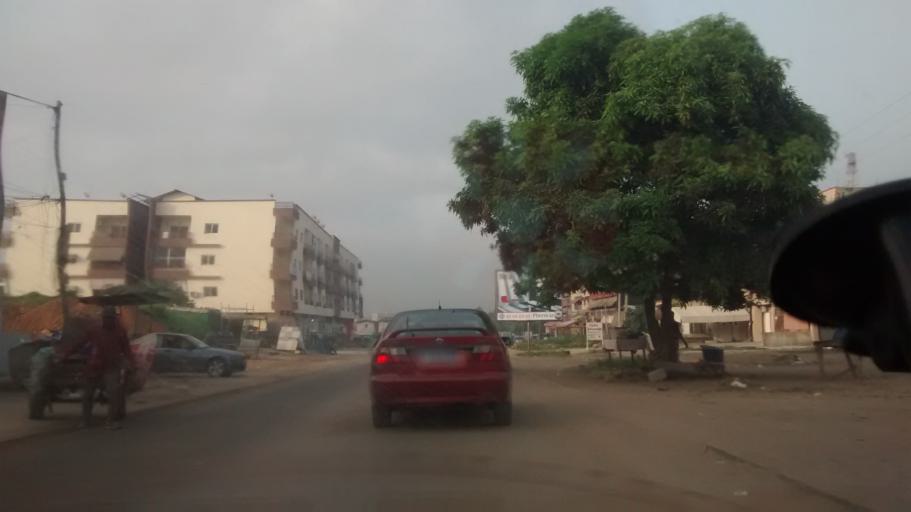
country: CI
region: Lagunes
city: Abobo
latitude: 5.4108
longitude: -3.9840
